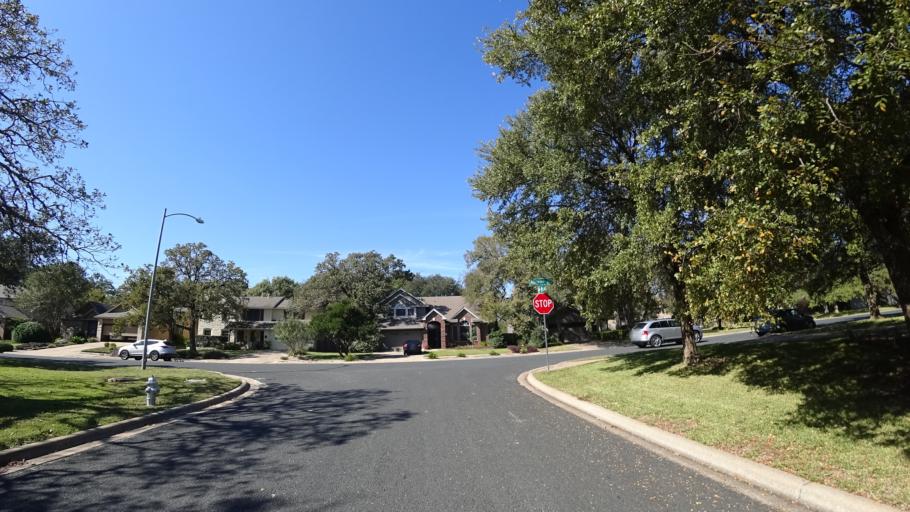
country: US
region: Texas
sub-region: Travis County
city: Shady Hollow
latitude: 30.2192
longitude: -97.8692
